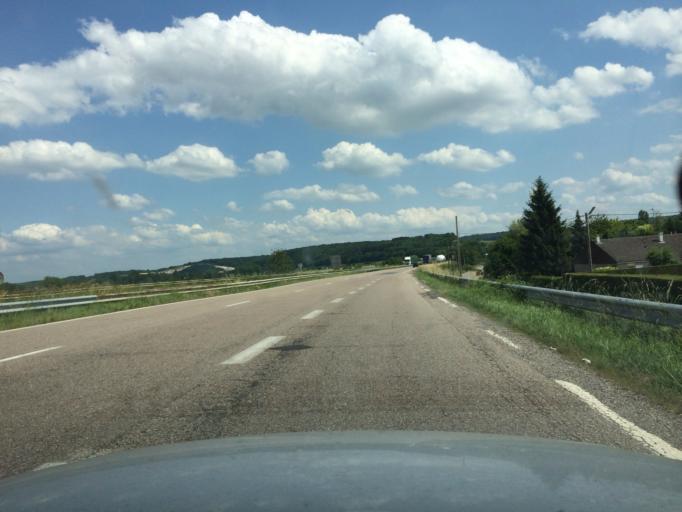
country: FR
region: Lorraine
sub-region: Departement de la Meuse
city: Vacon
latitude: 48.6905
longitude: 5.6253
